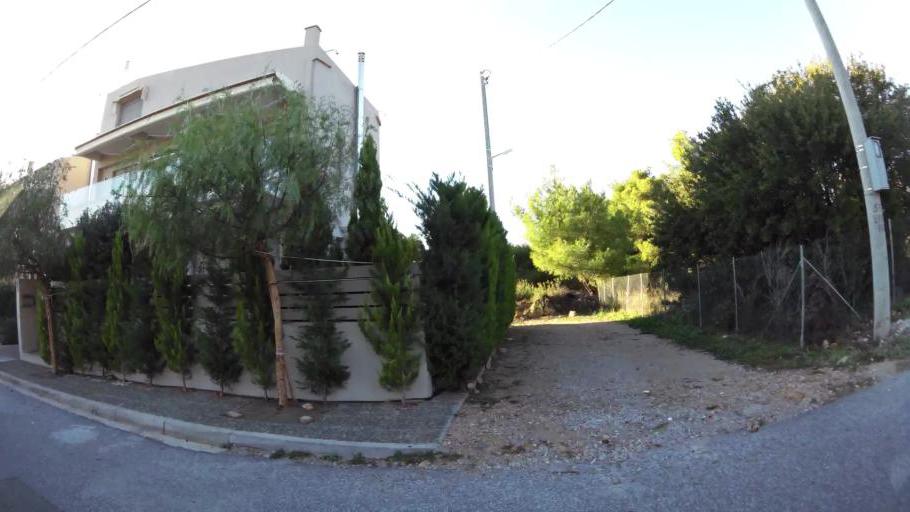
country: GR
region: Attica
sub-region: Nomarchia Athinas
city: Penteli
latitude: 38.0446
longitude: 23.8523
